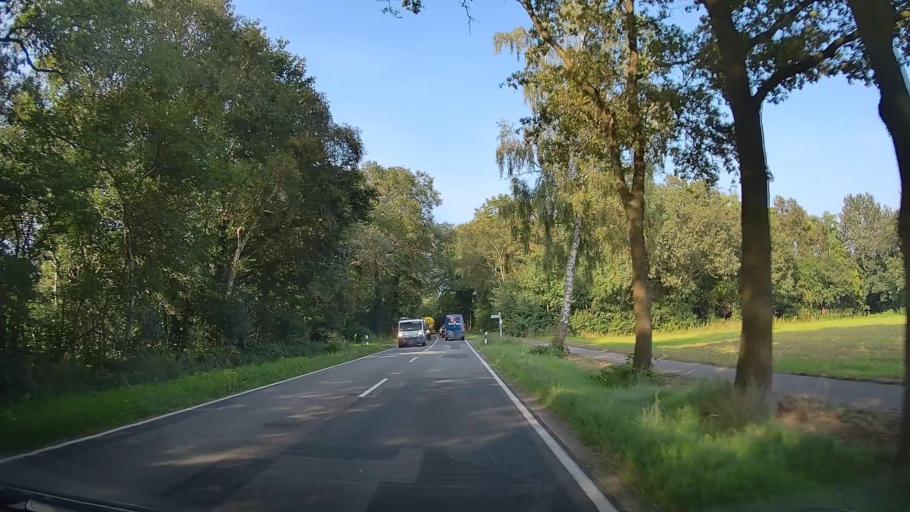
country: DE
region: Lower Saxony
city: Friesoythe
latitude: 53.0895
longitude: 7.8332
